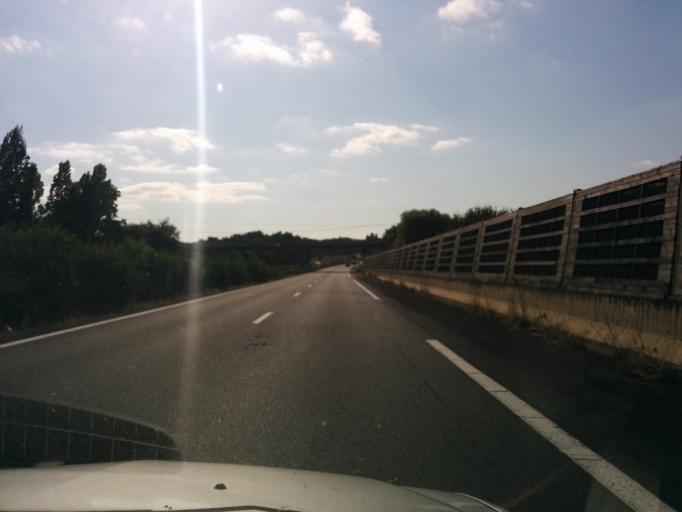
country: FR
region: Pays de la Loire
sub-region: Departement de la Loire-Atlantique
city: La Haie-Fouassiere
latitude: 47.1723
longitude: -1.3905
